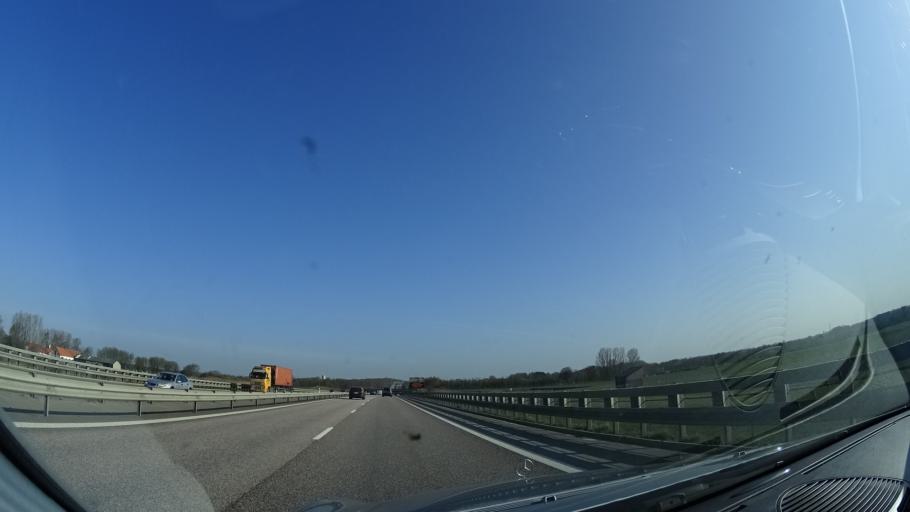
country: SE
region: Skane
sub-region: Helsingborg
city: Gantofta
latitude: 55.9928
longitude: 12.7802
